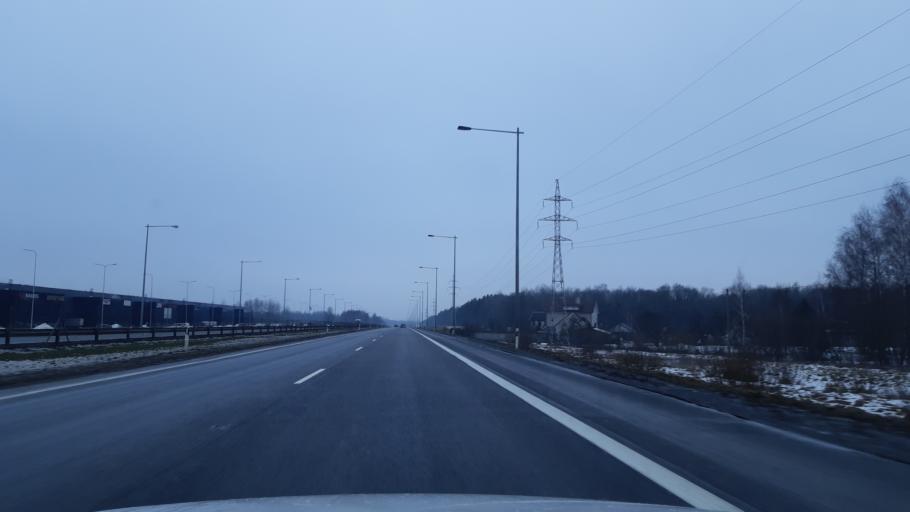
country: LT
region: Kauno apskritis
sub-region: Kaunas
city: Eiguliai
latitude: 54.9351
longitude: 23.9535
